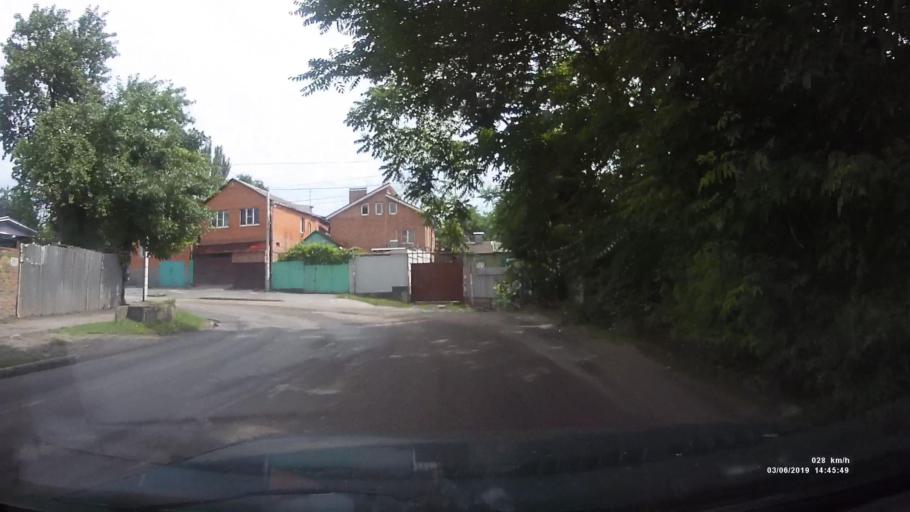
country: RU
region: Rostov
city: Rostov-na-Donu
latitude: 47.2468
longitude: 39.7235
